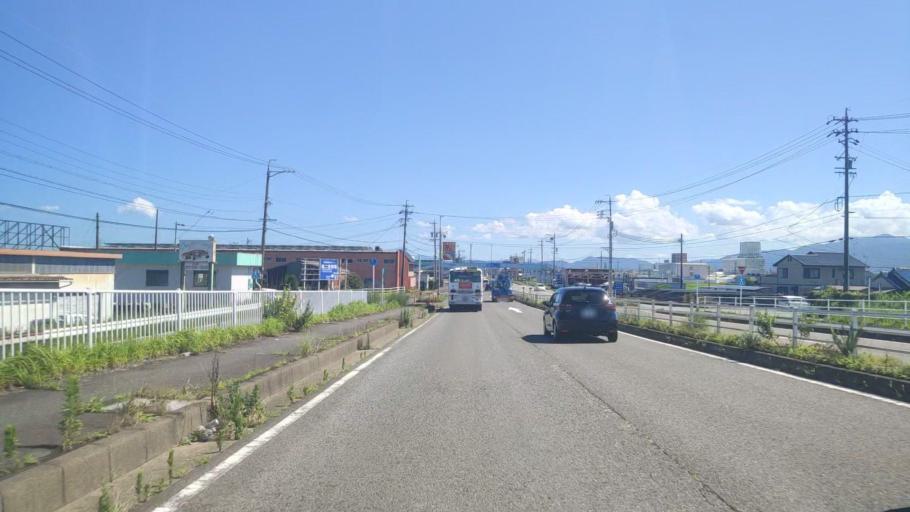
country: JP
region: Mie
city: Hisai-motomachi
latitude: 34.6440
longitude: 136.5187
